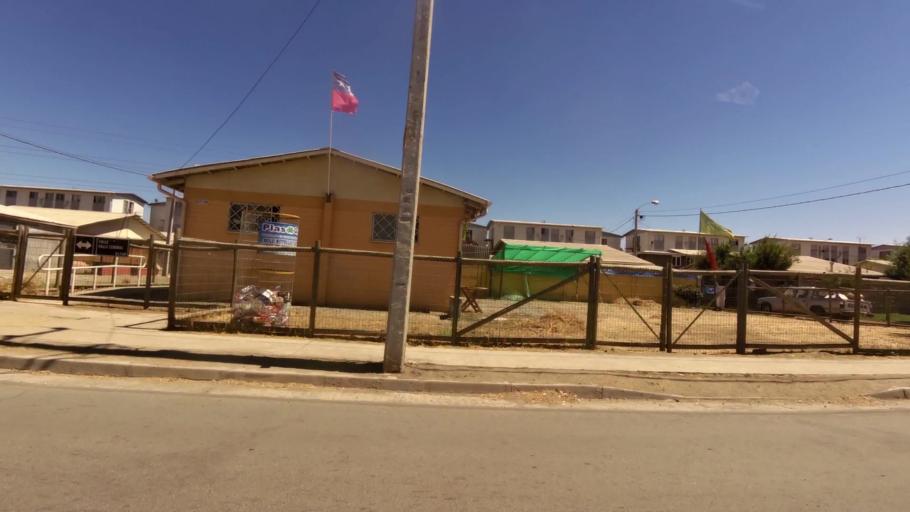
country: CL
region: O'Higgins
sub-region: Provincia de Cachapoal
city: Rancagua
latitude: -34.1450
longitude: -70.7255
